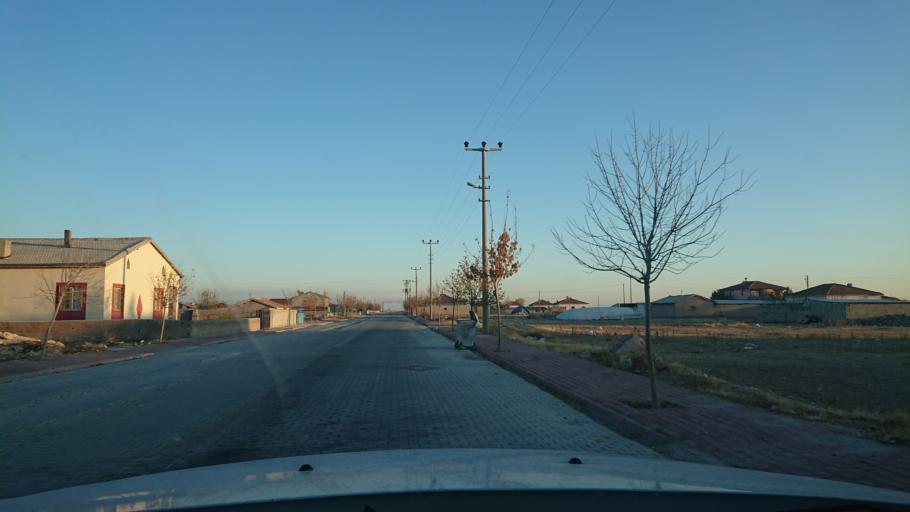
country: TR
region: Aksaray
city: Eskil
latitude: 38.3953
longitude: 33.4235
